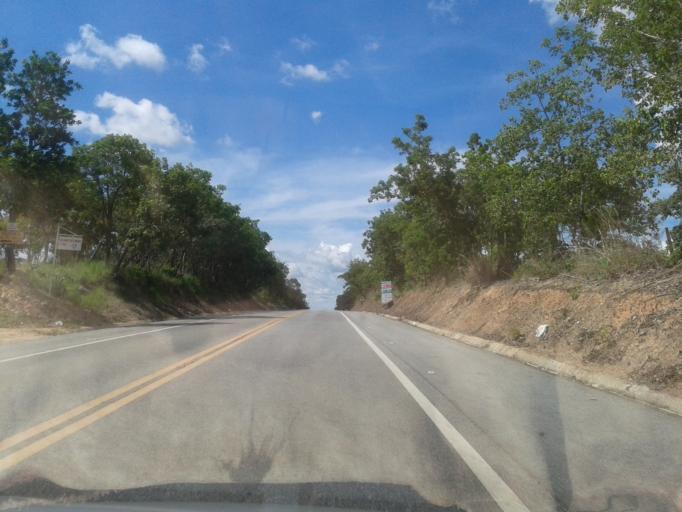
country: BR
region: Goias
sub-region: Goias
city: Goias
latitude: -15.7274
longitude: -50.1860
